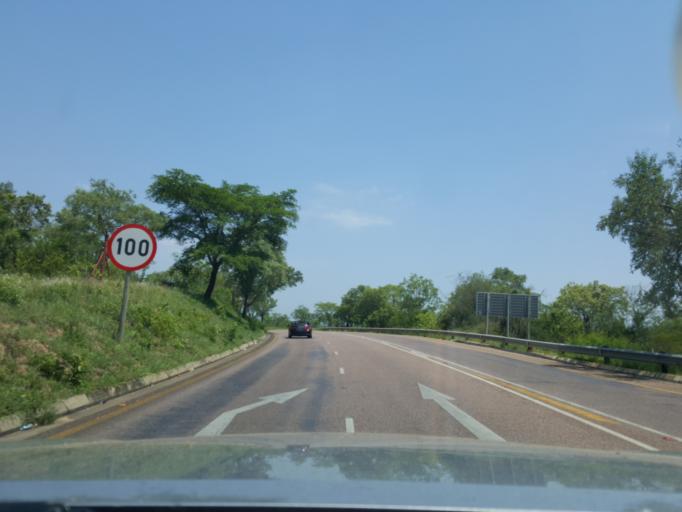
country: ZA
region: Mpumalanga
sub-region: Ehlanzeni District
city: Graksop
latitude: -25.0241
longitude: 31.1236
